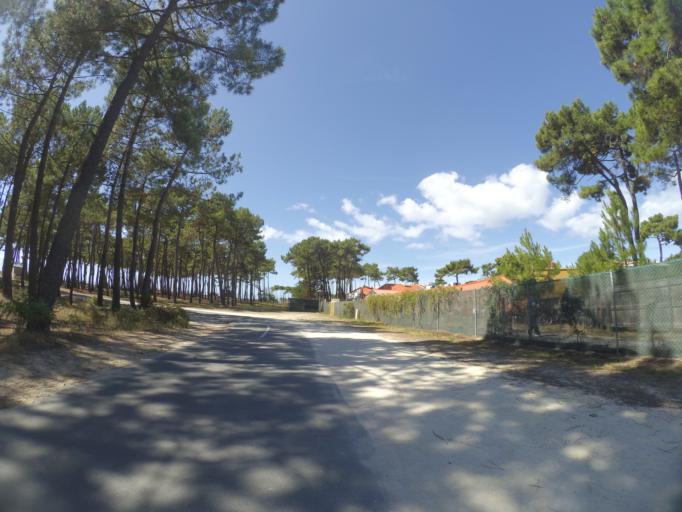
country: FR
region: Poitou-Charentes
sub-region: Departement de la Charente-Maritime
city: Les Mathes
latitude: 45.6777
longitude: -1.1614
